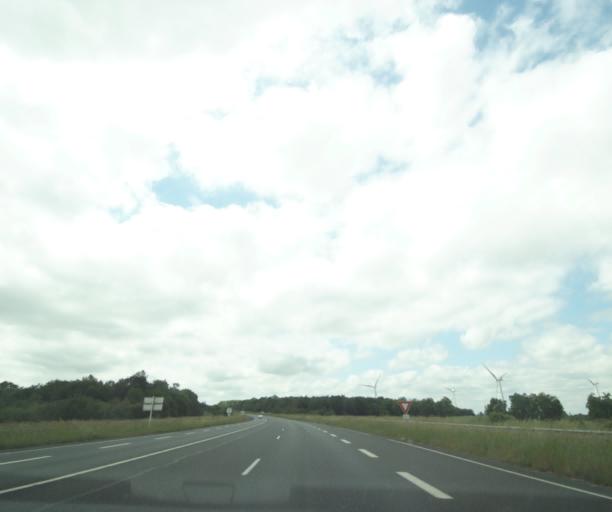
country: FR
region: Poitou-Charentes
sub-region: Departement des Deux-Sevres
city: Saint-Varent
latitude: 46.8661
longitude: -0.2061
